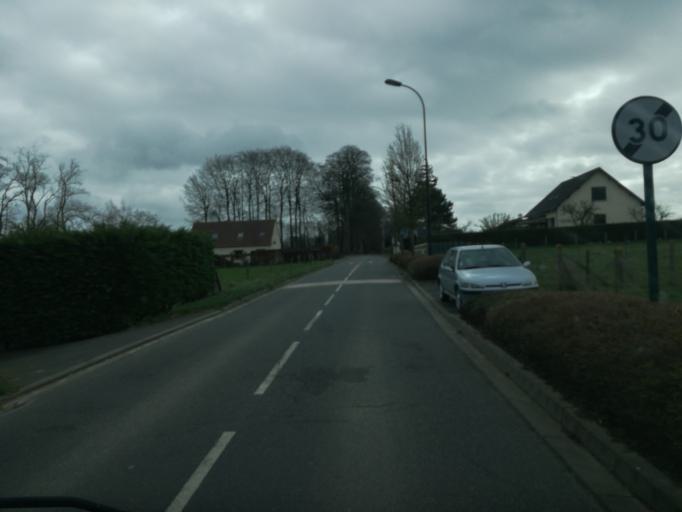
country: FR
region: Haute-Normandie
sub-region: Departement de la Seine-Maritime
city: Yebleron
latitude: 49.6652
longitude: 0.5036
